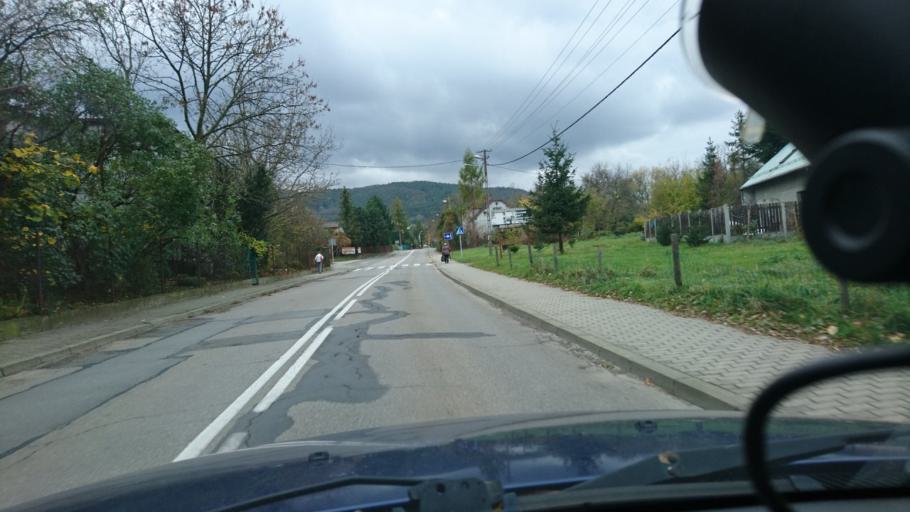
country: PL
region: Silesian Voivodeship
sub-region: Bielsko-Biala
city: Bielsko-Biala
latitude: 49.7970
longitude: 19.0153
